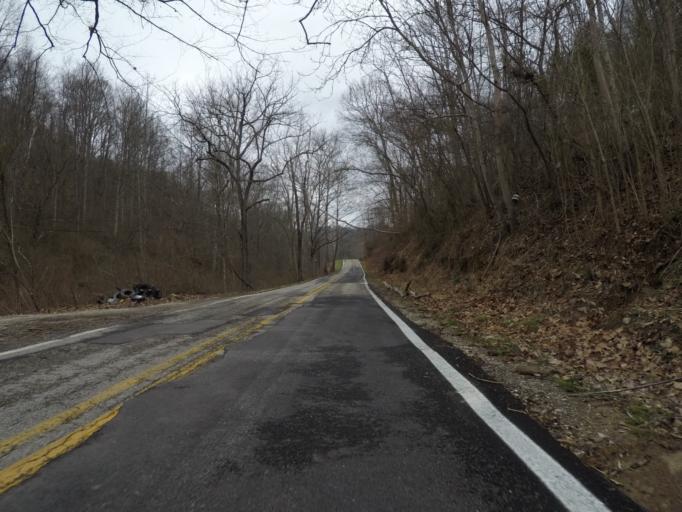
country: US
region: West Virginia
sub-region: Cabell County
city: Lesage
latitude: 38.4633
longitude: -82.2774
